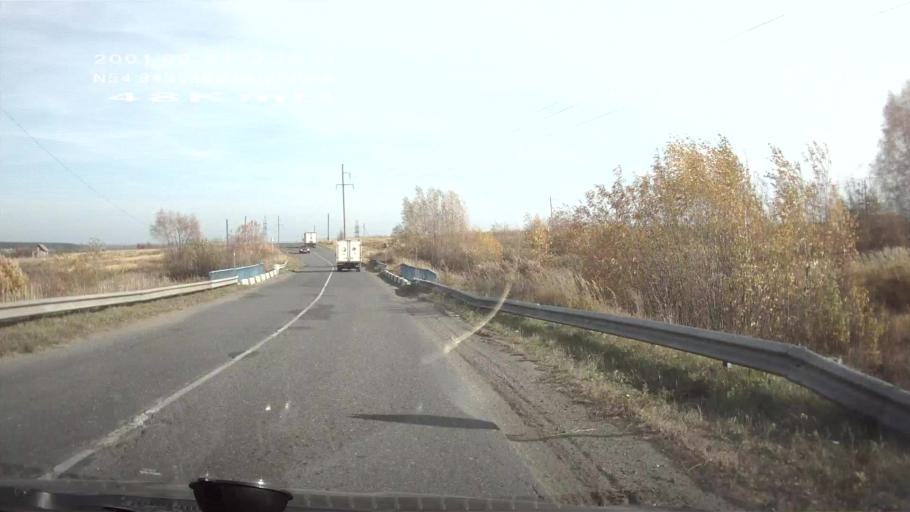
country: RU
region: Chuvashia
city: Alatyr'
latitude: 54.8431
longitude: 46.4761
